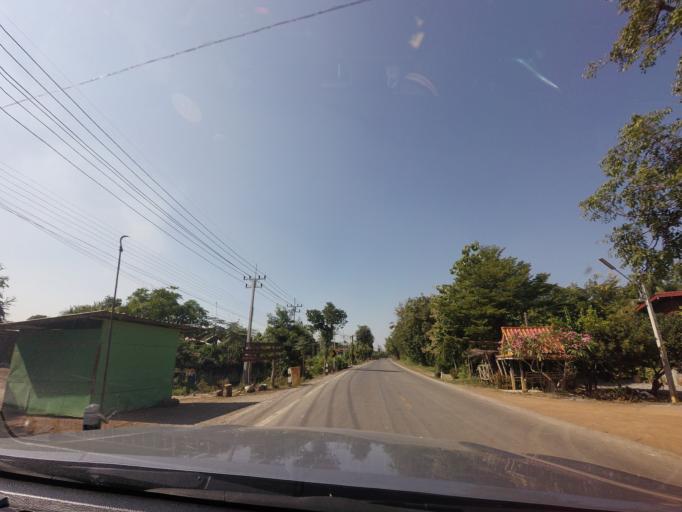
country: TH
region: Sukhothai
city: Sawankhalok
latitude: 17.3648
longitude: 99.8069
